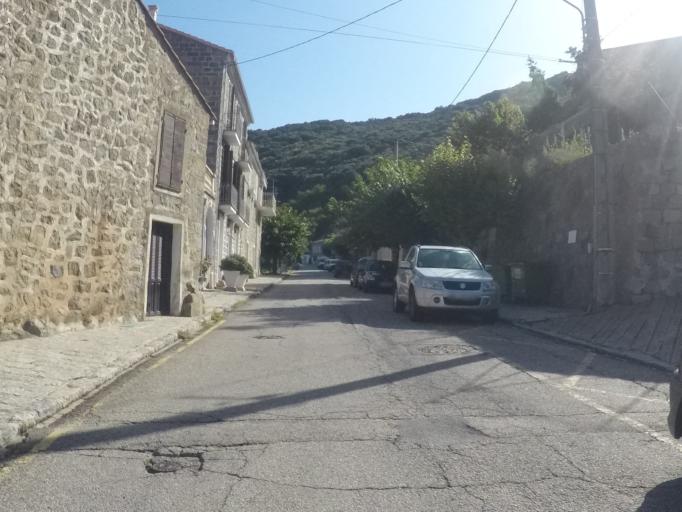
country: FR
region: Corsica
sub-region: Departement de la Corse-du-Sud
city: Olmeto
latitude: 41.7449
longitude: 8.9122
